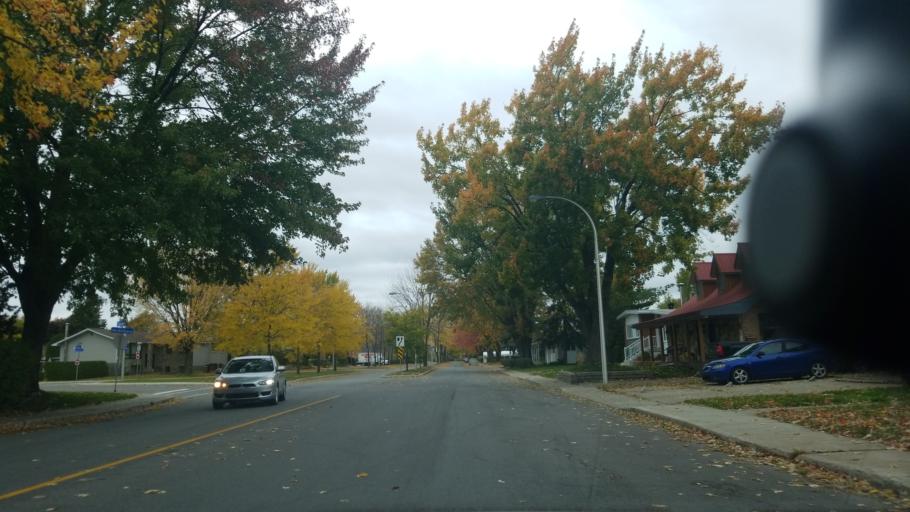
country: CA
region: Quebec
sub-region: Laval
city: Laval
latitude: 45.5760
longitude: -73.7291
